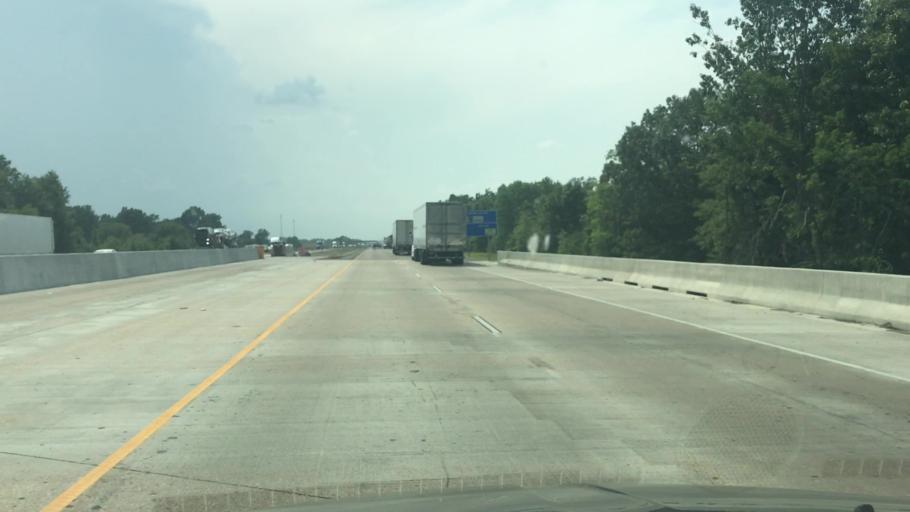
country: US
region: Arkansas
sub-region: Crittenden County
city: Earle
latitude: 35.1339
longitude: -90.4539
